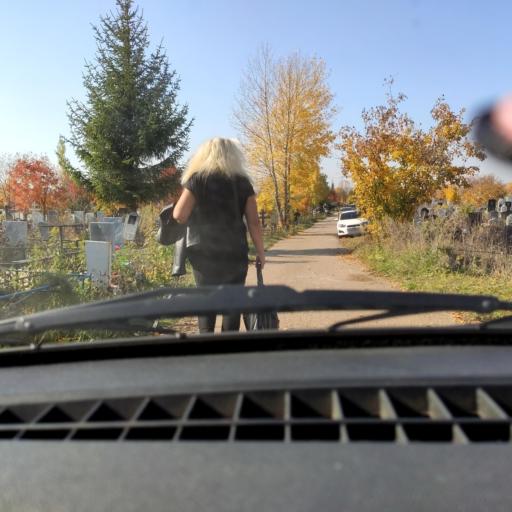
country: RU
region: Bashkortostan
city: Mikhaylovka
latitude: 54.8158
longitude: 55.8690
